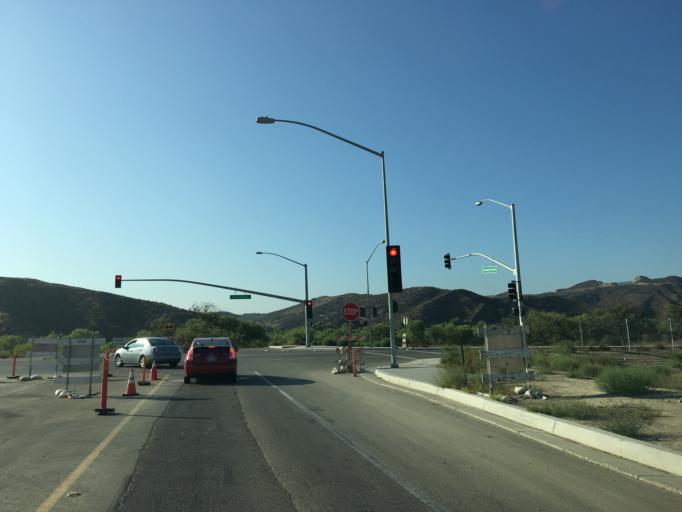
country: US
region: California
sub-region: Los Angeles County
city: Valencia
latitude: 34.4344
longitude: -118.6175
